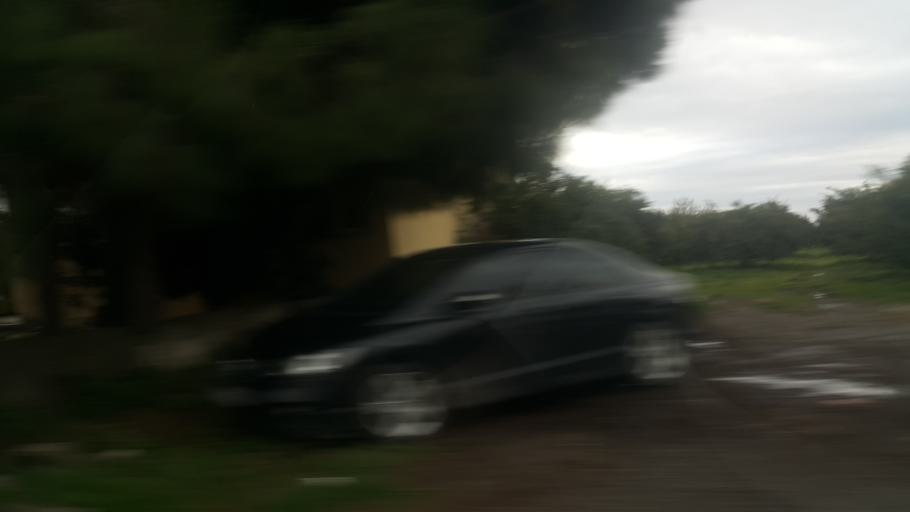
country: TR
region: Izmir
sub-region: Seferihisar
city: Seferhisar
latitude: 38.1940
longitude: 26.8303
